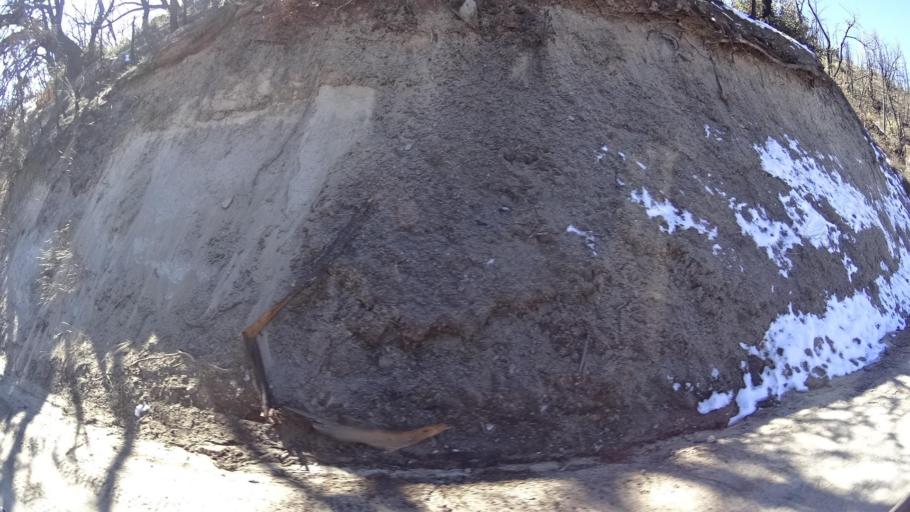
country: US
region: California
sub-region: Kern County
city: Alta Sierra
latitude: 35.7171
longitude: -118.5282
